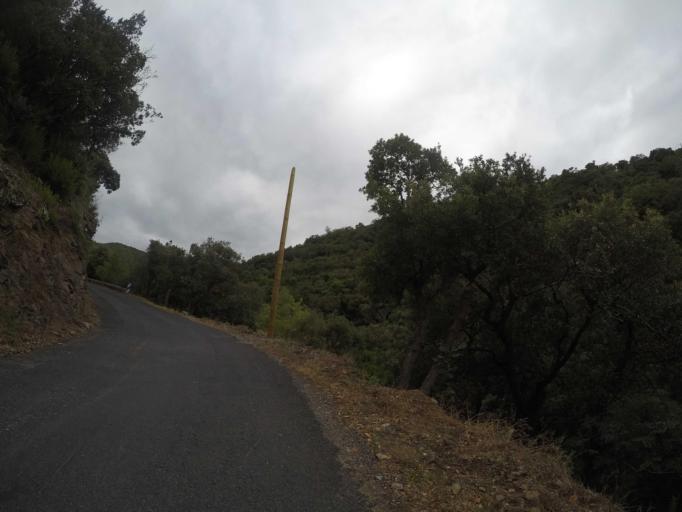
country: FR
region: Languedoc-Roussillon
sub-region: Departement des Pyrenees-Orientales
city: Ille-sur-Tet
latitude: 42.6385
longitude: 2.6205
